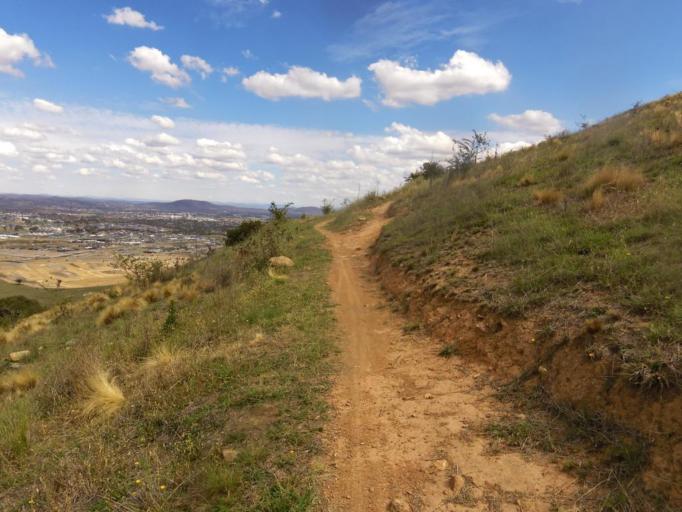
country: AU
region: Australian Capital Territory
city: Belconnen
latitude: -35.1417
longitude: 149.0933
